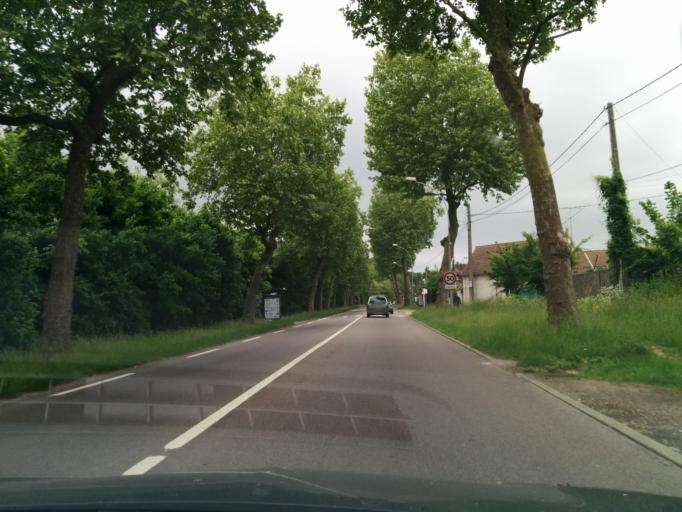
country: FR
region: Ile-de-France
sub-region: Departement des Yvelines
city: Rosny-sur-Seine
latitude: 49.0031
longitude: 1.6250
